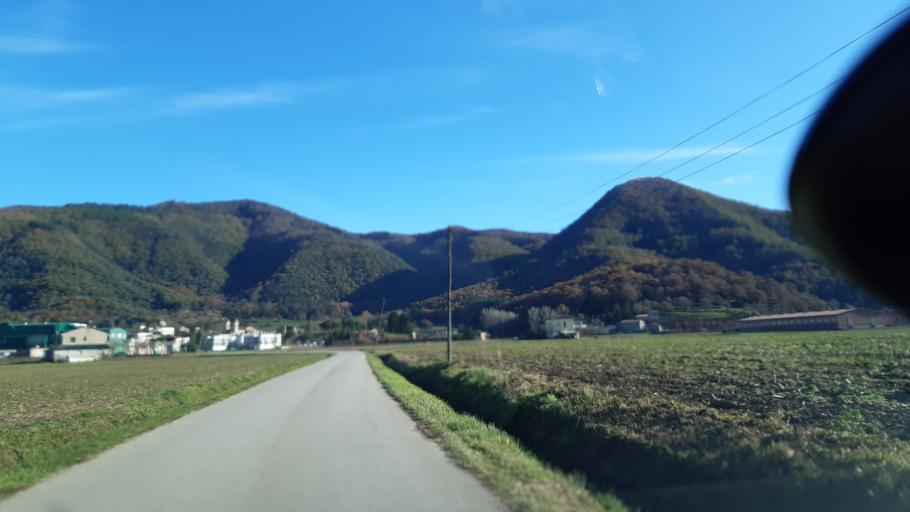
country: ES
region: Catalonia
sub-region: Provincia de Girona
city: Bas
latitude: 42.1433
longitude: 2.4516
